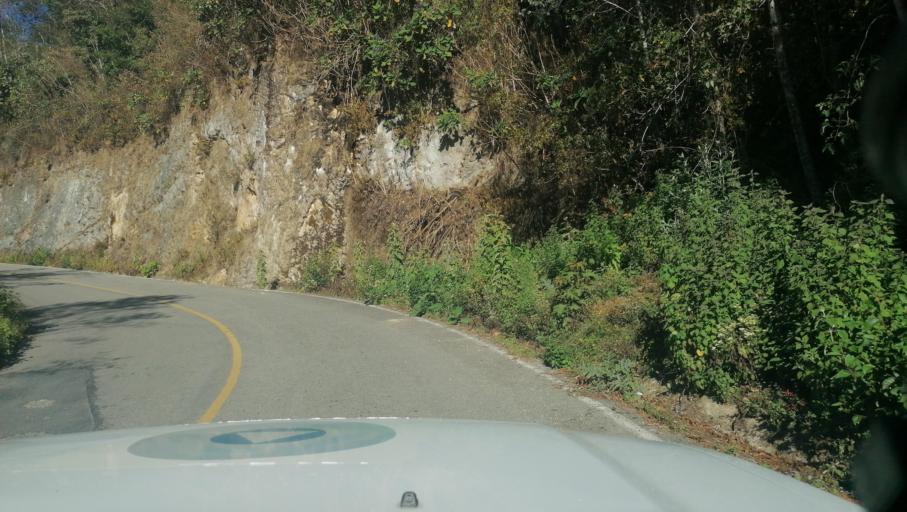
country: MX
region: Chiapas
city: Motozintla de Mendoza
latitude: 15.2367
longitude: -92.2355
